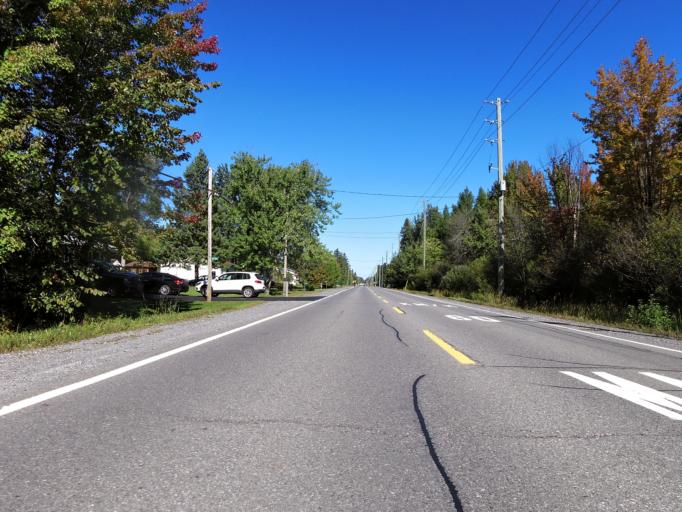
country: CA
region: Ontario
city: Clarence-Rockland
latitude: 45.3615
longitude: -75.4521
